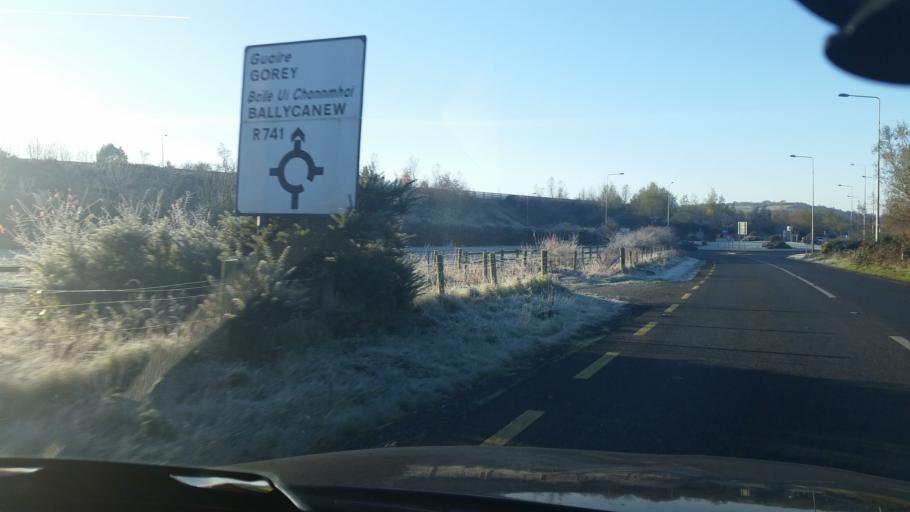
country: IE
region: Leinster
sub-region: Loch Garman
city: Gorey
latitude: 52.6626
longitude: -6.2809
